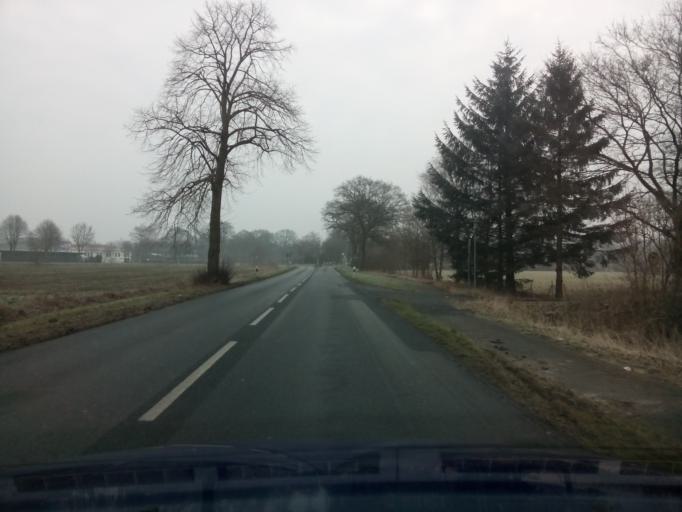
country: DE
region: Lower Saxony
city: Flogeln
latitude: 53.6248
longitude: 8.8144
